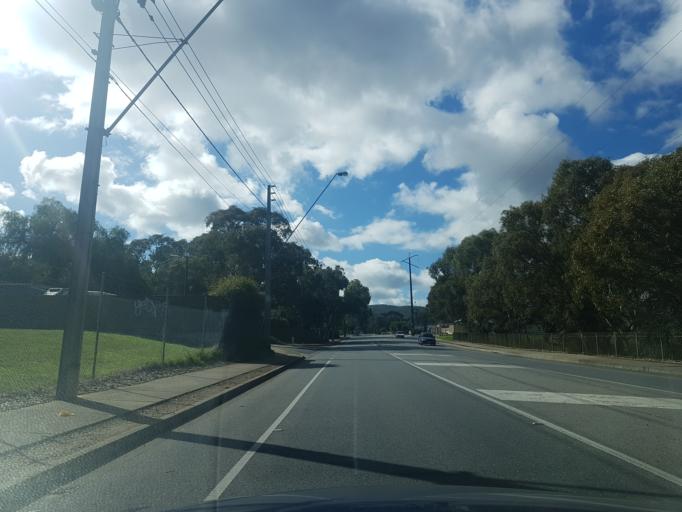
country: AU
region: South Australia
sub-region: Tea Tree Gully
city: Hope Valley
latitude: -34.8327
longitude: 138.6992
